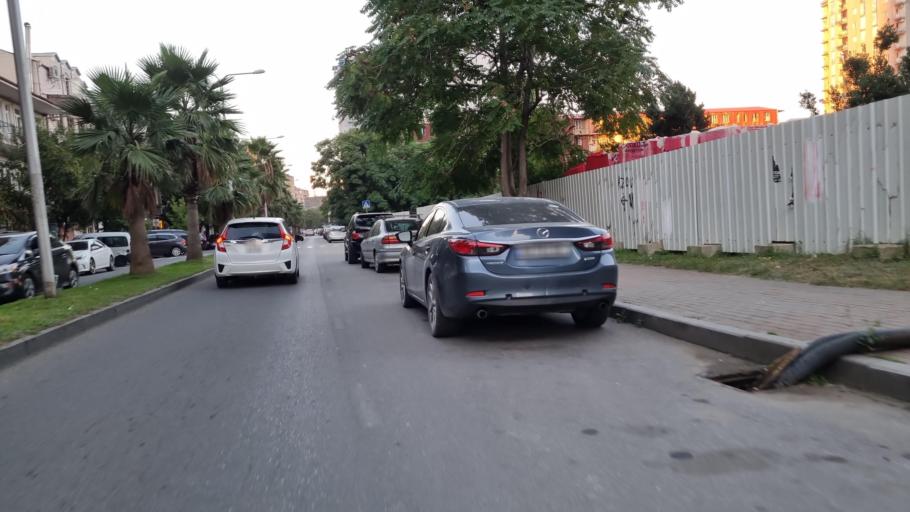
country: GE
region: Ajaria
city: Batumi
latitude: 41.6407
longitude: 41.6175
